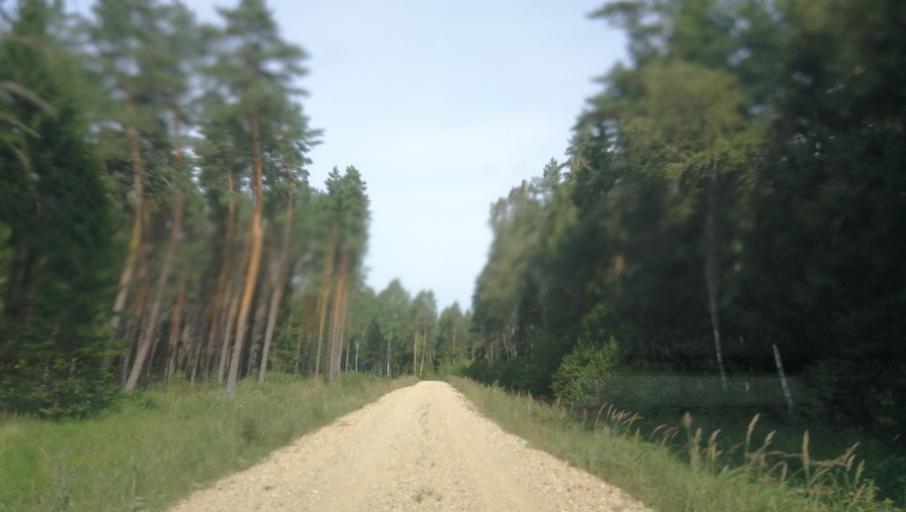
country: LV
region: Pavilostas
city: Pavilosta
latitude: 56.8123
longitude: 21.3362
